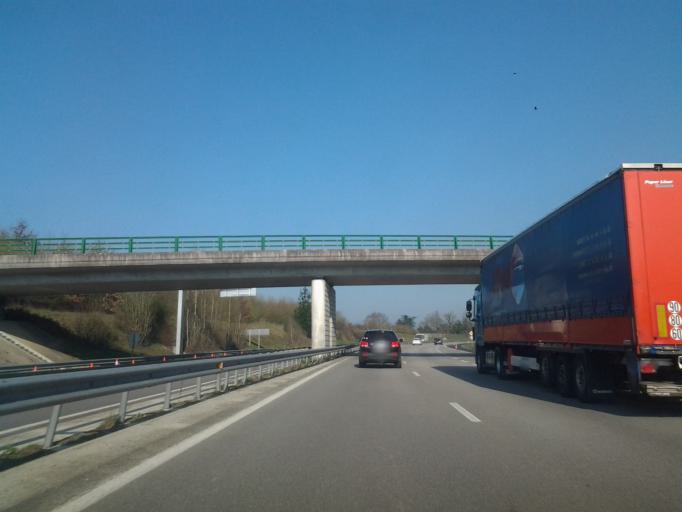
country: FR
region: Pays de la Loire
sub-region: Departement de la Vendee
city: Aizenay
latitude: 46.7375
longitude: -1.6201
